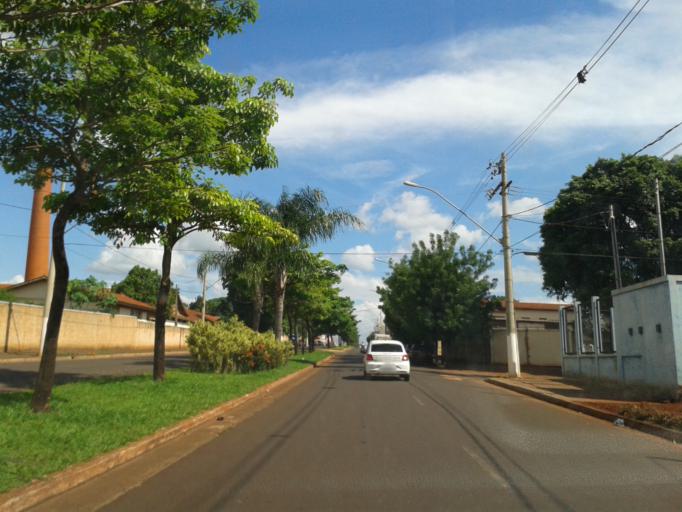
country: BR
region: Minas Gerais
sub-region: Ituiutaba
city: Ituiutaba
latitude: -18.9763
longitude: -49.4828
